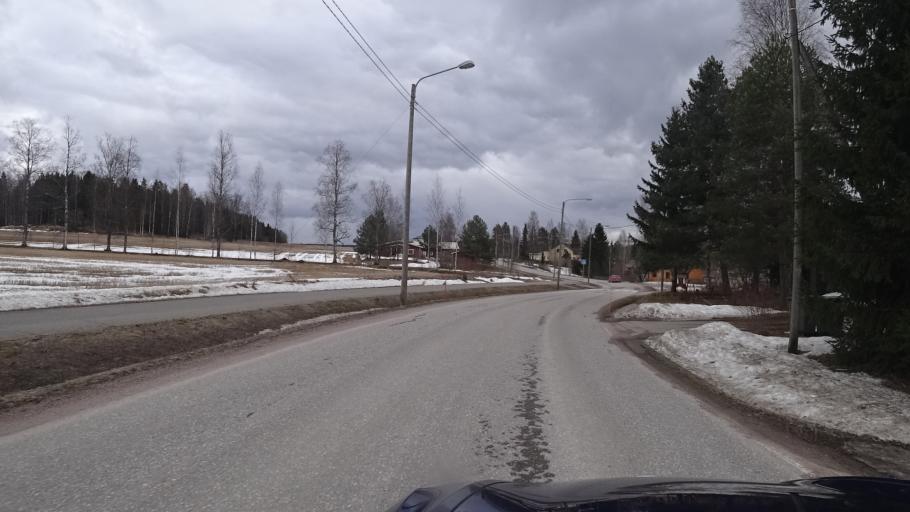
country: FI
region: Paijanne Tavastia
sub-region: Lahti
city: Nastola
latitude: 60.8717
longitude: 26.0093
